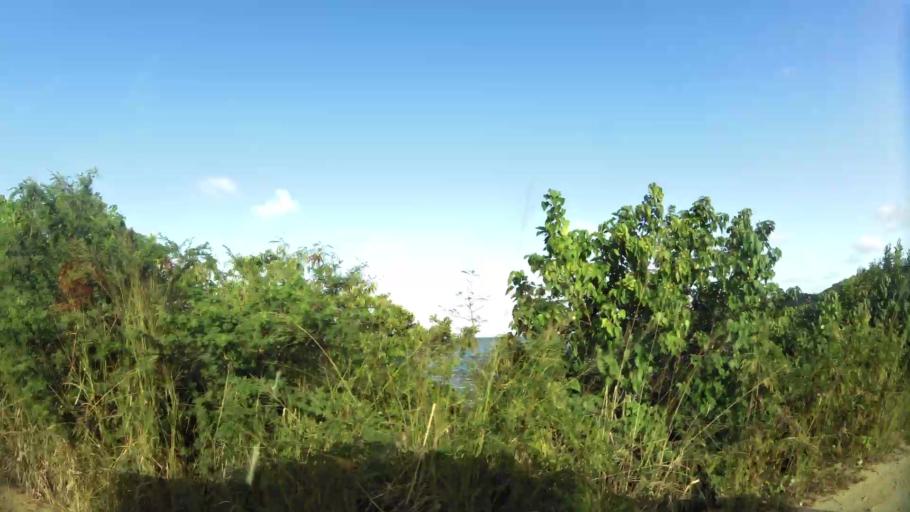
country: AG
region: Saint George
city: Piggotts
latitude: 17.1239
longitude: -61.7882
